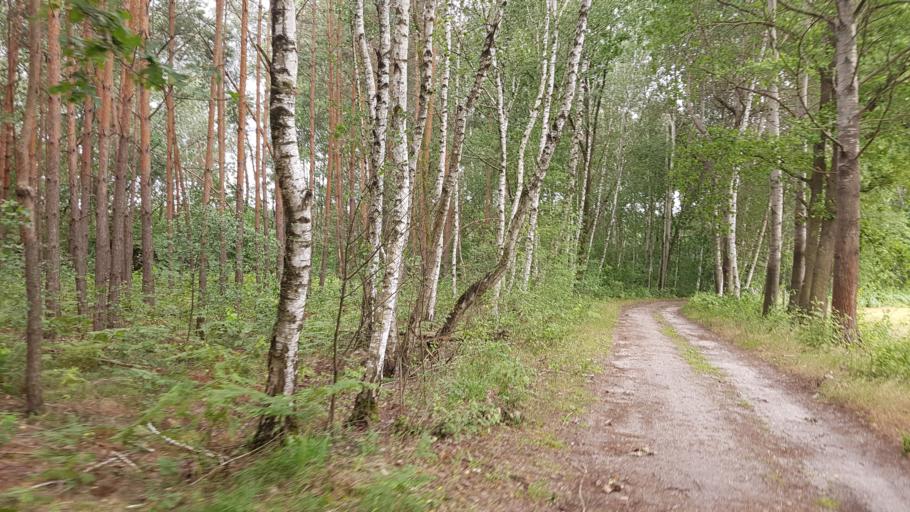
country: DE
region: Brandenburg
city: Doberlug-Kirchhain
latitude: 51.6347
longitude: 13.6013
